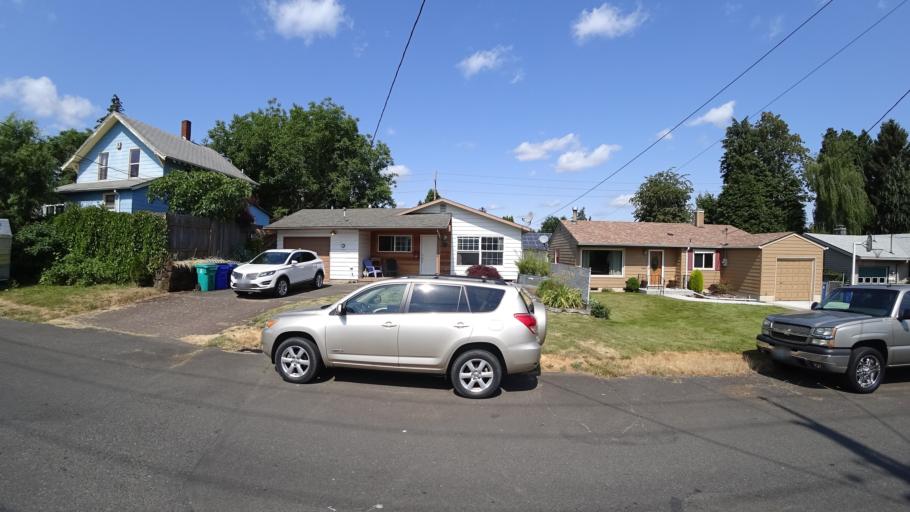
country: US
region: Oregon
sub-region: Washington County
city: West Haven
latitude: 45.5979
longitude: -122.7441
